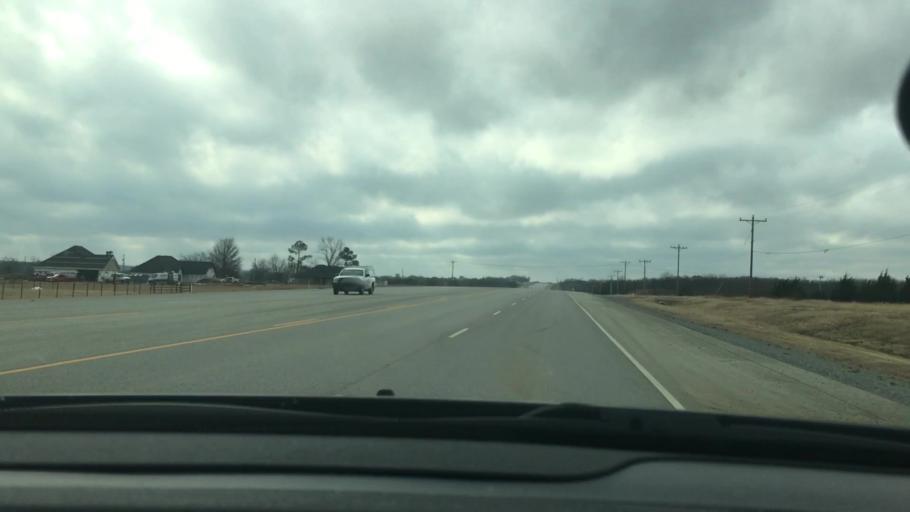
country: US
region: Oklahoma
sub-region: Bryan County
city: Durant
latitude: 34.0730
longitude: -96.3731
